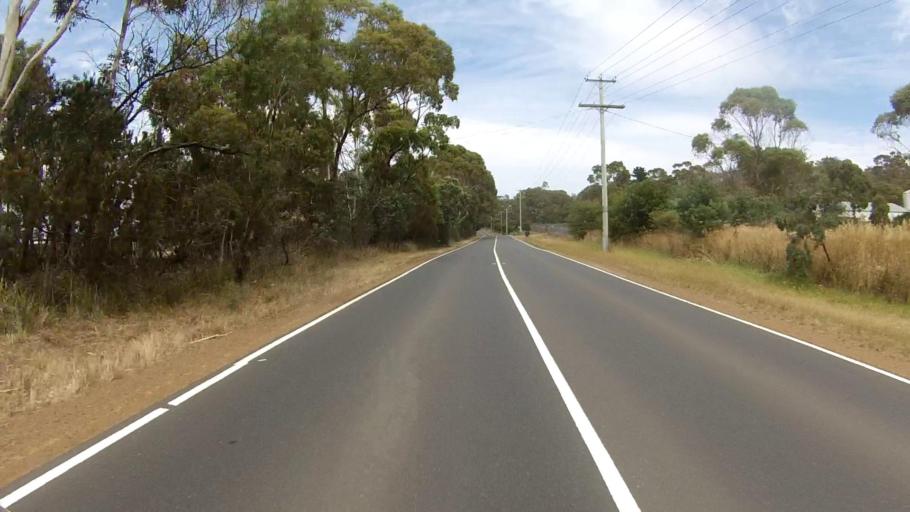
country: AU
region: Tasmania
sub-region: Clarence
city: Acton Park
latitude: -42.8764
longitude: 147.4827
